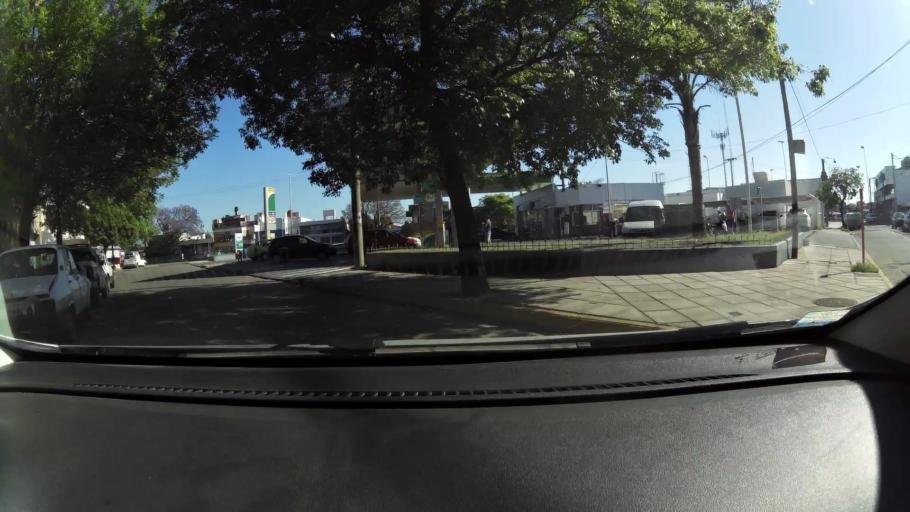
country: AR
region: Cordoba
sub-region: Departamento de Capital
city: Cordoba
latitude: -31.4335
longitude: -64.1593
